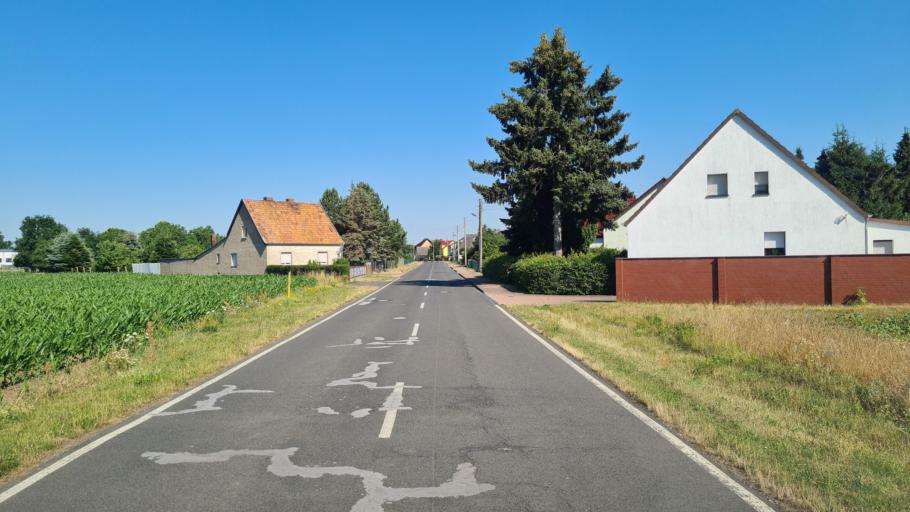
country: DE
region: Saxony-Anhalt
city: Annaburg
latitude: 51.6955
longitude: 12.9905
